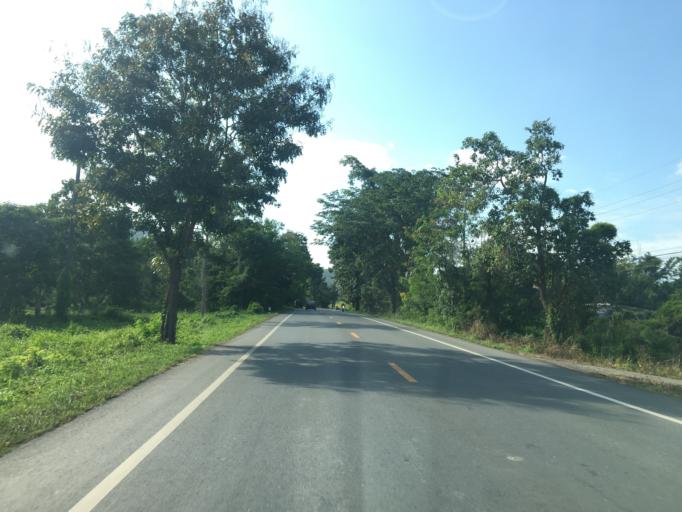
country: TH
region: Phayao
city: Chun
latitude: 19.3512
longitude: 100.1059
